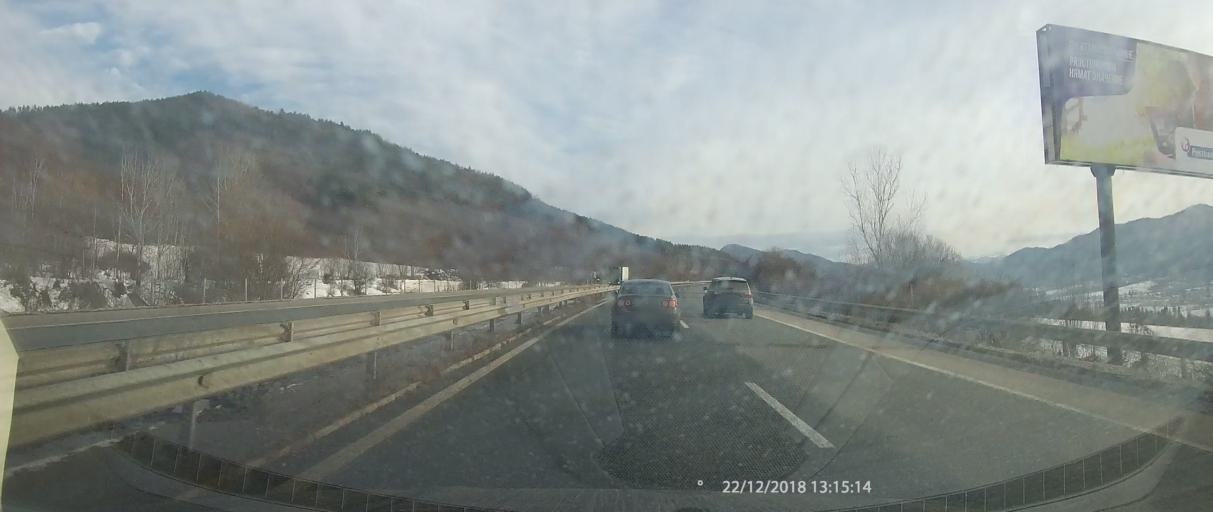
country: BG
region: Sofiya
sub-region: Obshtina Pravets
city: Pravets
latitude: 42.9147
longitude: 23.8994
